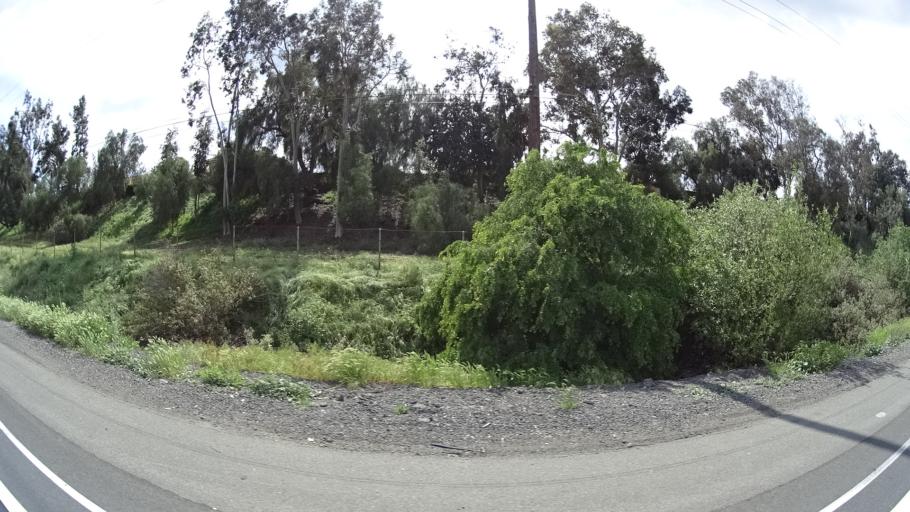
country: US
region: California
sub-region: Los Angeles County
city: Pomona
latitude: 34.0406
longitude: -117.7678
